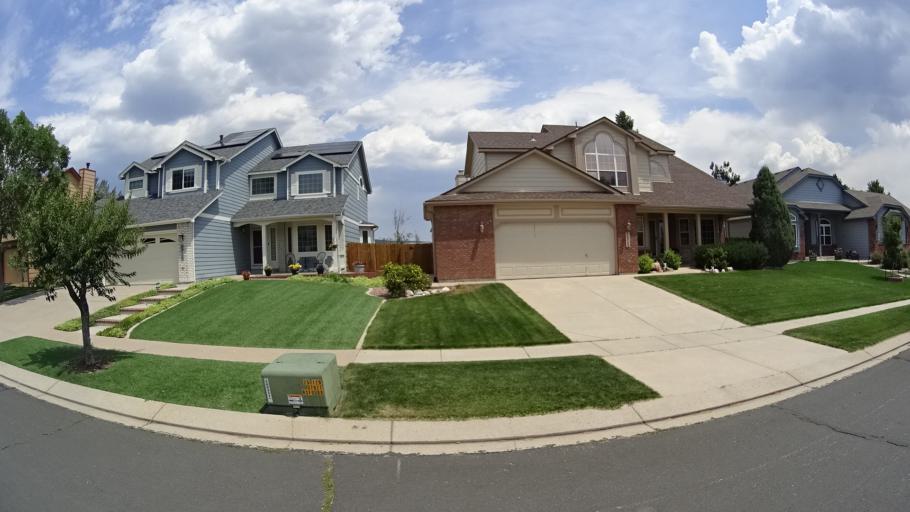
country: US
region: Colorado
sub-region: El Paso County
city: Black Forest
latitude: 38.9634
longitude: -104.7691
